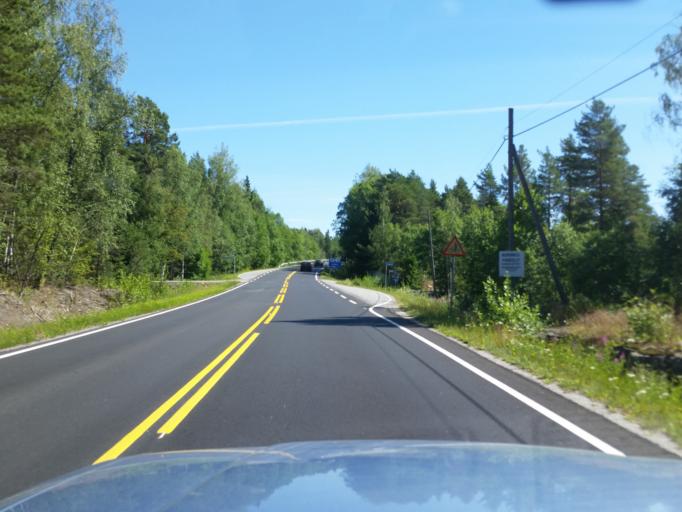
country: FI
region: Varsinais-Suomi
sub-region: Aboland-Turunmaa
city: Laensi-Turunmaa
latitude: 60.2532
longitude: 22.2356
